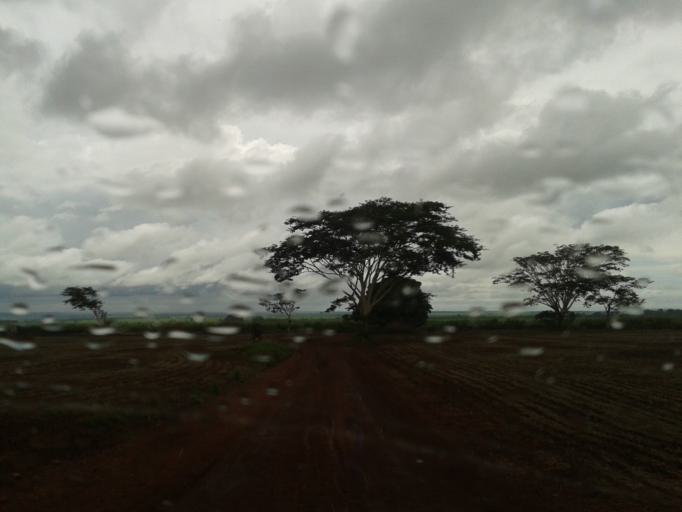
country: BR
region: Minas Gerais
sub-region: Santa Vitoria
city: Santa Vitoria
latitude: -18.6599
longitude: -49.9121
